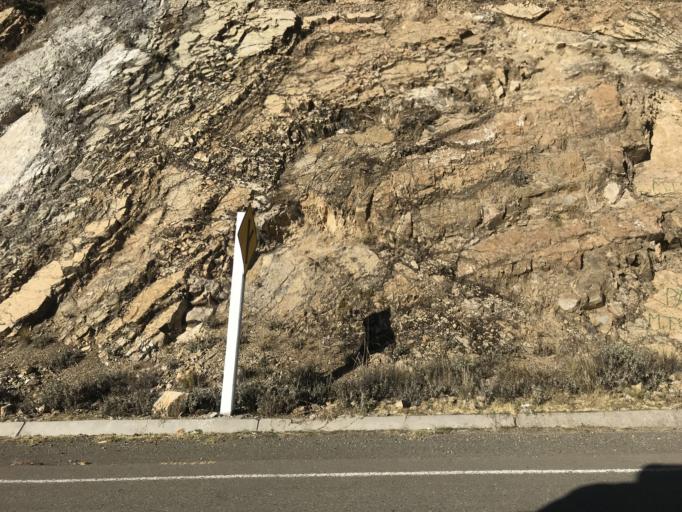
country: BO
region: La Paz
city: San Pedro
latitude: -16.2261
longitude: -68.8489
